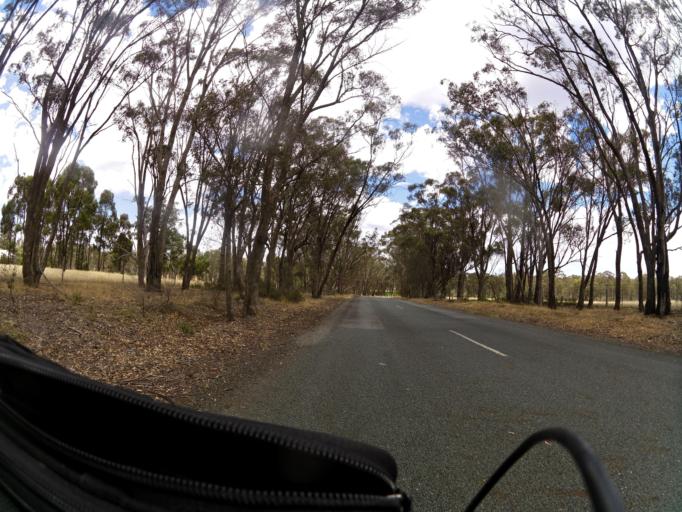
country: AU
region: Victoria
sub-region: Greater Shepparton
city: Shepparton
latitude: -36.6826
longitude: 145.1902
